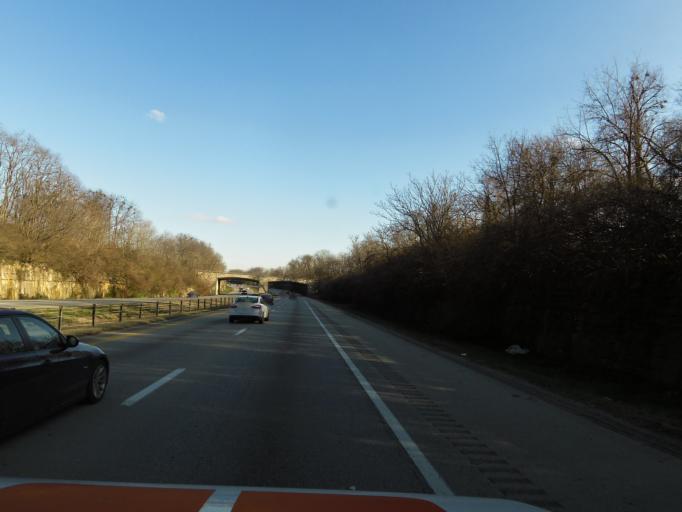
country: US
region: Kentucky
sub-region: Jefferson County
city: Saint Matthews
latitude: 38.2401
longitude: -85.6779
